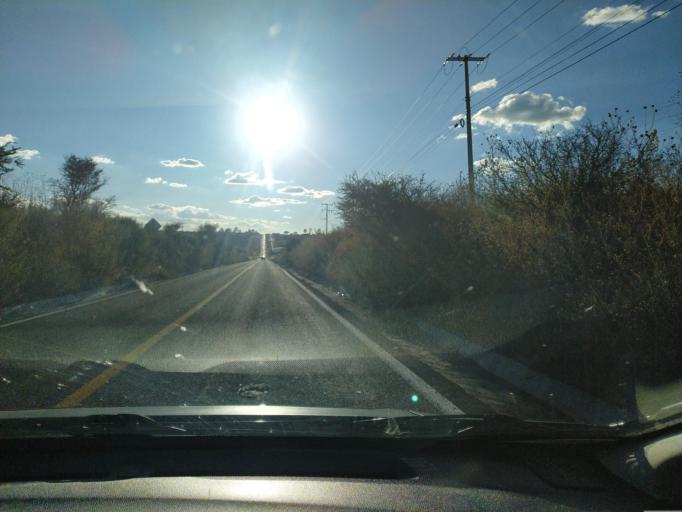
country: MX
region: Jalisco
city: San Diego de Alejandria
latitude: 21.0180
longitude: -101.9550
